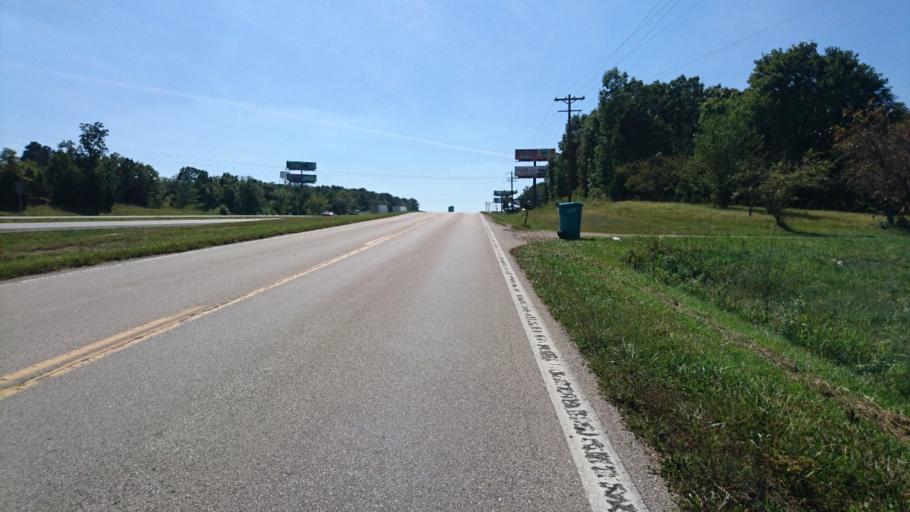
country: US
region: Missouri
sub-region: Franklin County
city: Sullivan
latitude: 38.2318
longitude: -91.1495
